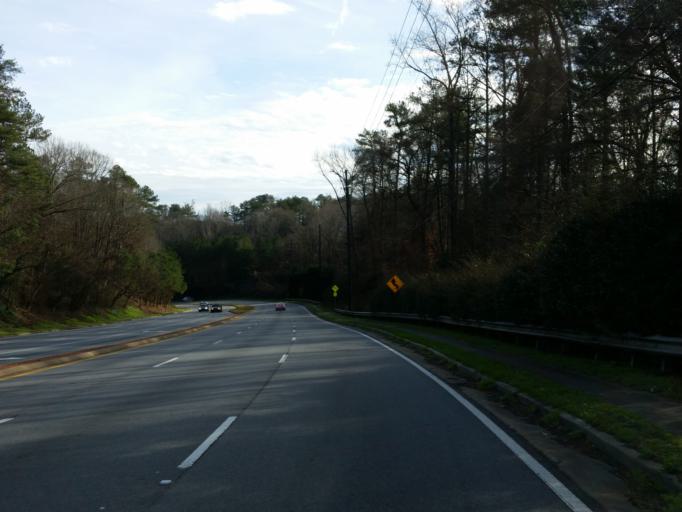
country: US
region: Georgia
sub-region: Fulton County
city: Sandy Springs
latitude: 33.9493
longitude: -84.4112
